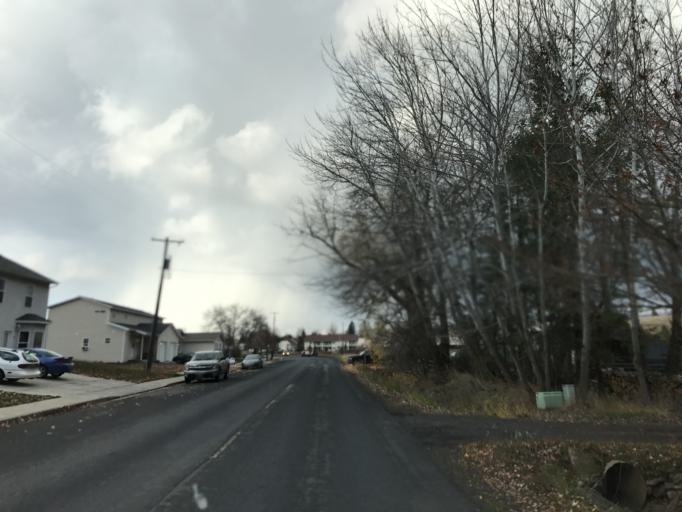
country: US
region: Idaho
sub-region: Latah County
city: Moscow
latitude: 46.7434
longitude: -116.9941
